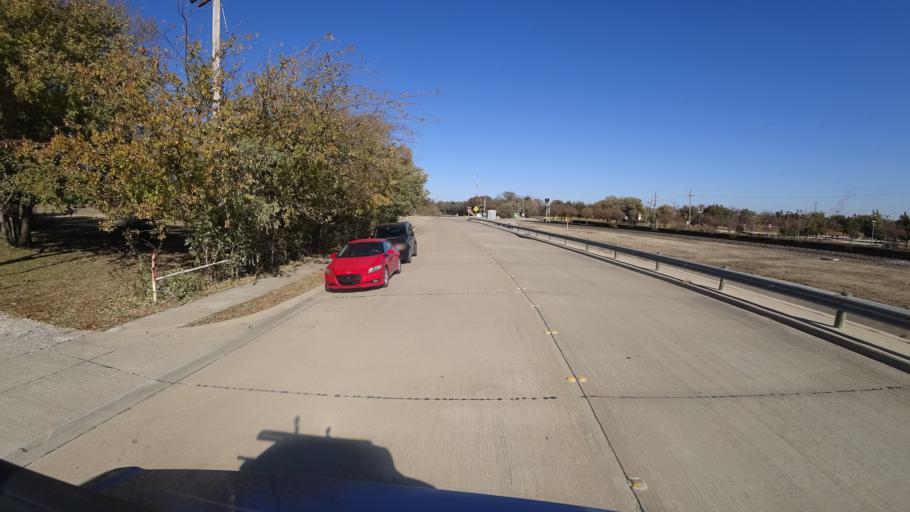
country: US
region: Texas
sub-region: Denton County
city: Lewisville
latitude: 33.0481
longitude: -96.9871
